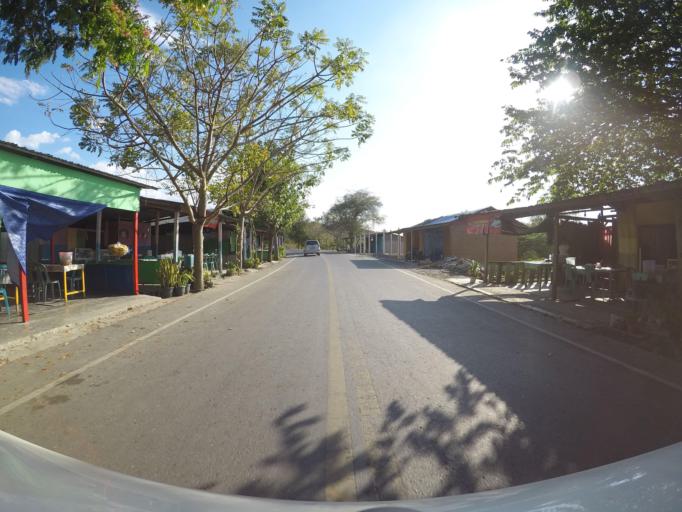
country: TL
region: Liquica
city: Maubara
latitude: -8.7390
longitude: 125.1347
